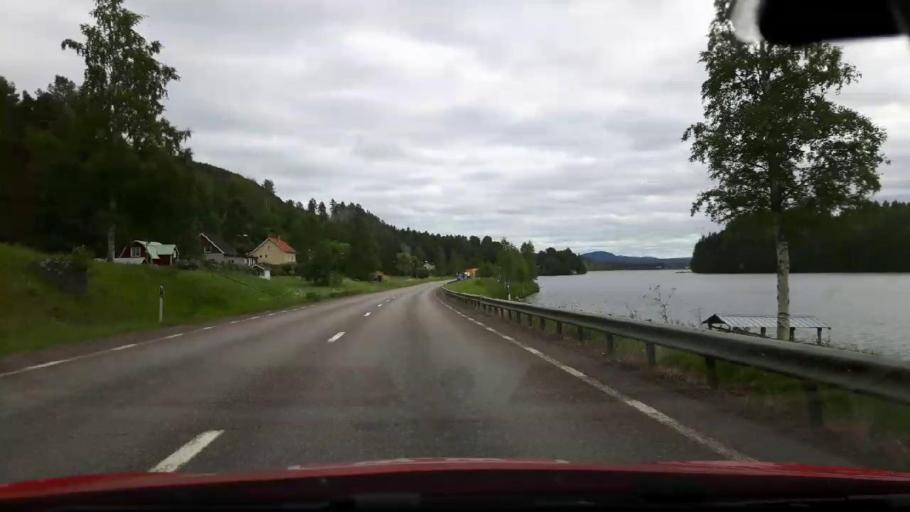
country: SE
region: Jaemtland
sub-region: Ragunda Kommun
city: Hammarstrand
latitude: 63.1416
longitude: 16.3371
